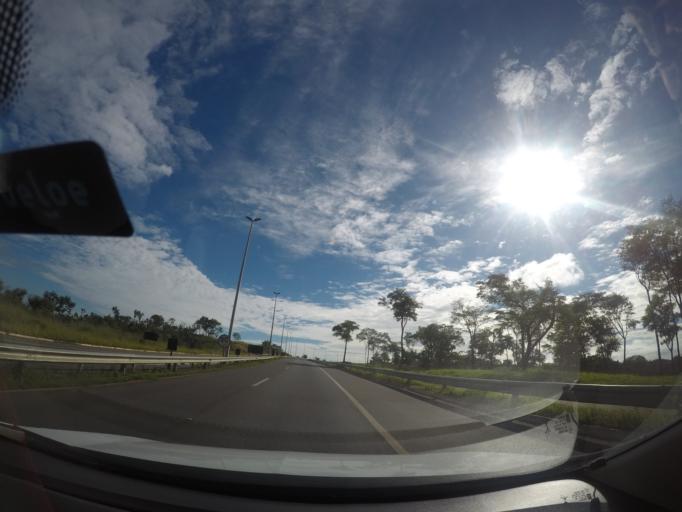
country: BR
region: Goias
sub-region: Senador Canedo
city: Senador Canedo
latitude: -16.6881
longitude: -49.1653
